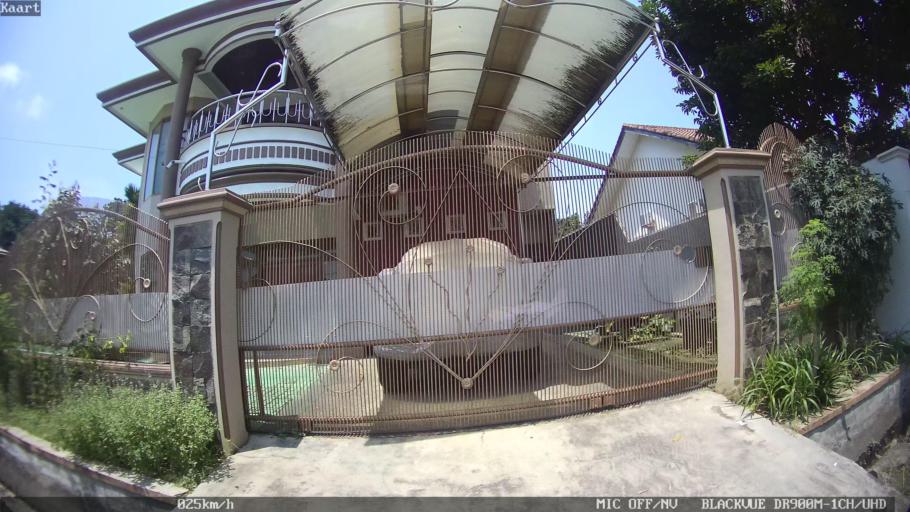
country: ID
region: Lampung
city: Kedaton
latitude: -5.3732
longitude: 105.2670
